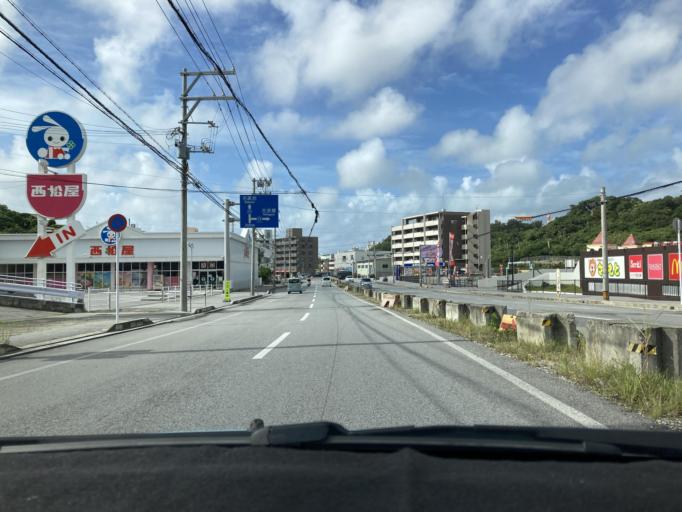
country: JP
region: Okinawa
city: Tomigusuku
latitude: 26.1893
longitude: 127.6889
